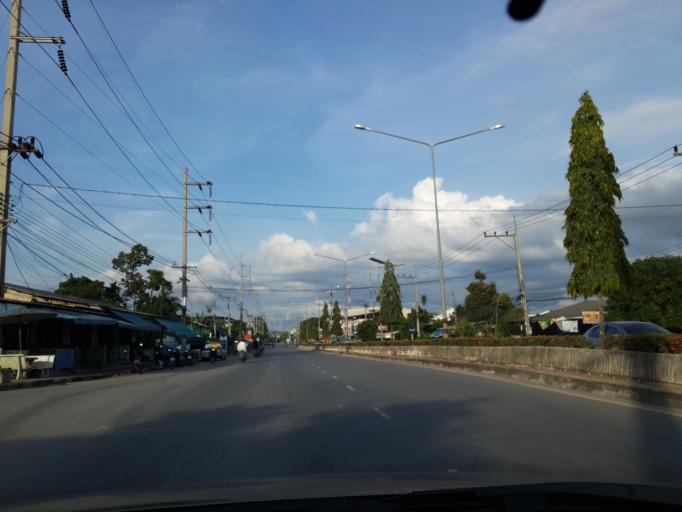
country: TH
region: Yala
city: Yala
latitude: 6.5424
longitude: 101.2702
